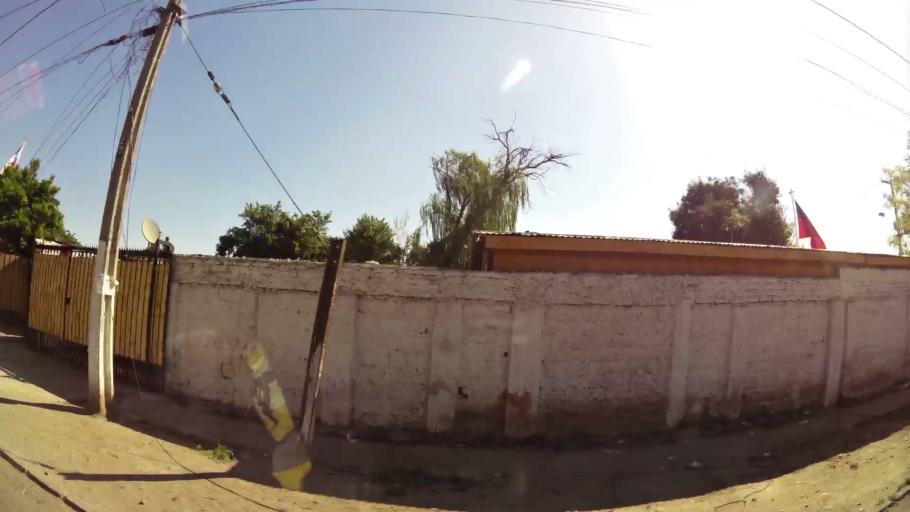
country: CL
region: Santiago Metropolitan
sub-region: Provincia de Santiago
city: La Pintana
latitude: -33.5395
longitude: -70.6197
